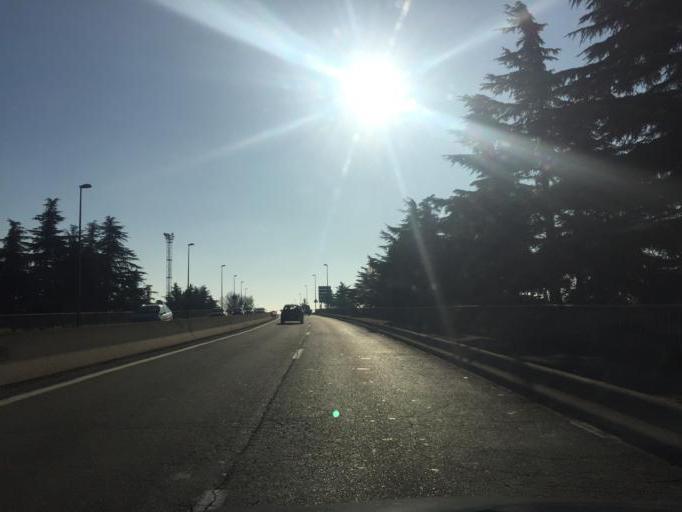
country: FR
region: Provence-Alpes-Cote d'Azur
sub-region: Departement du Vaucluse
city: Avignon
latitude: 43.9398
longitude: 4.8320
